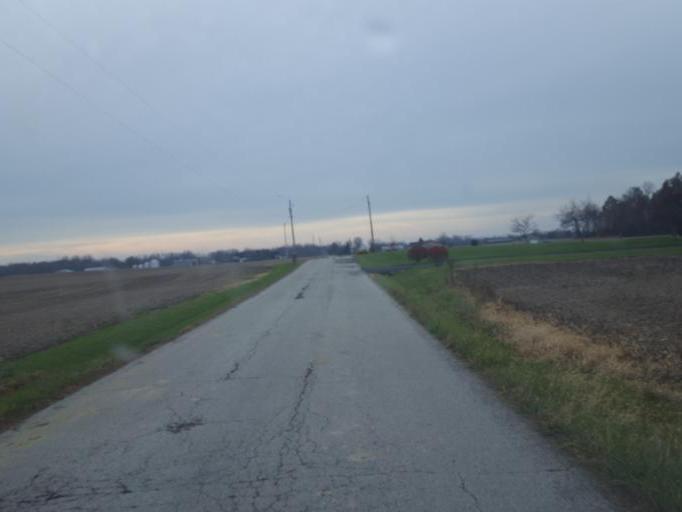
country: US
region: Ohio
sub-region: Morrow County
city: Cardington
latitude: 40.5246
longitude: -82.8776
